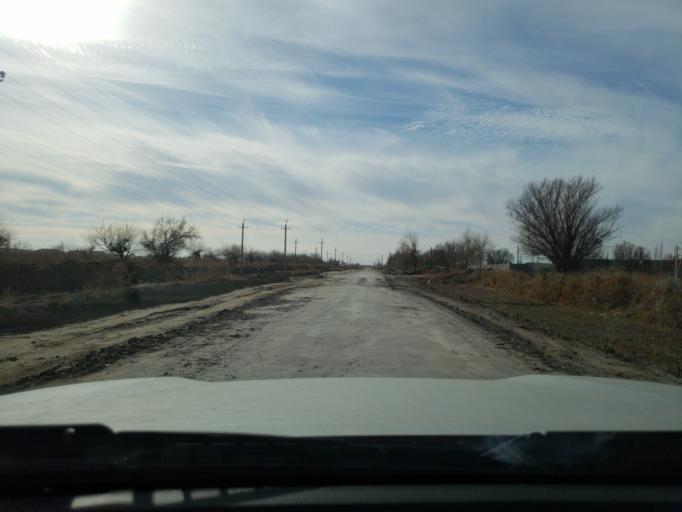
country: TM
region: Dasoguz
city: Dasoguz
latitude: 41.8475
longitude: 59.8791
